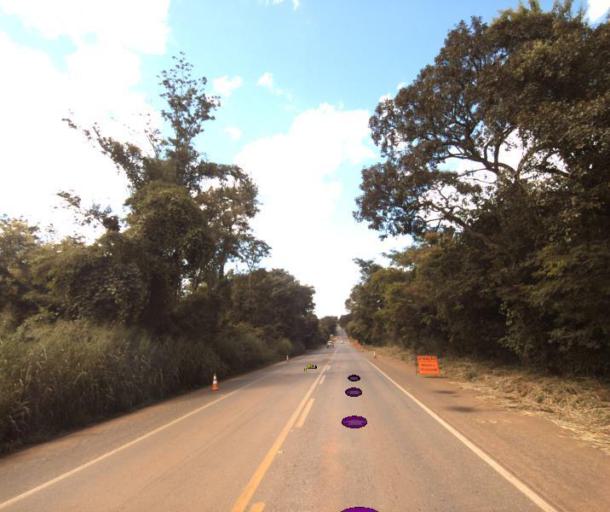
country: BR
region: Goias
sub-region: Petrolina De Goias
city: Petrolina de Goias
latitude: -16.0053
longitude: -49.1328
